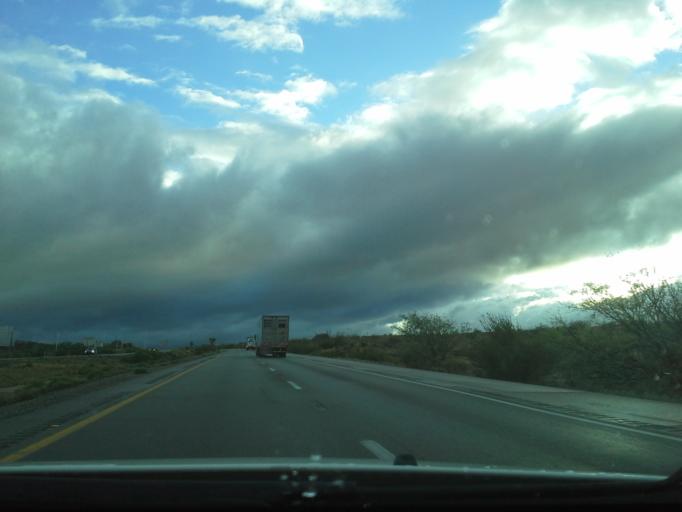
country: US
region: Arizona
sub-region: Cochise County
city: Whetstone
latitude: 31.9729
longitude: -110.3247
